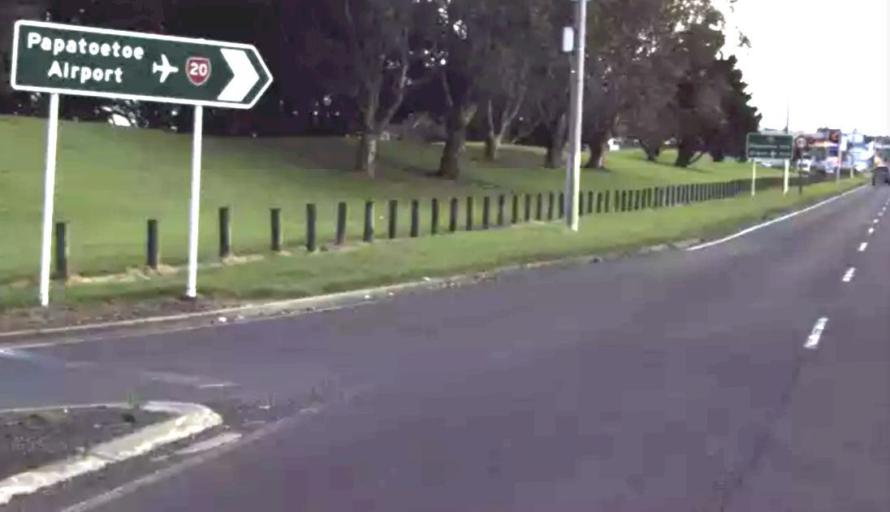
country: NZ
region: Auckland
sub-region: Auckland
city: Wiri
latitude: -37.0060
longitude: 174.8551
